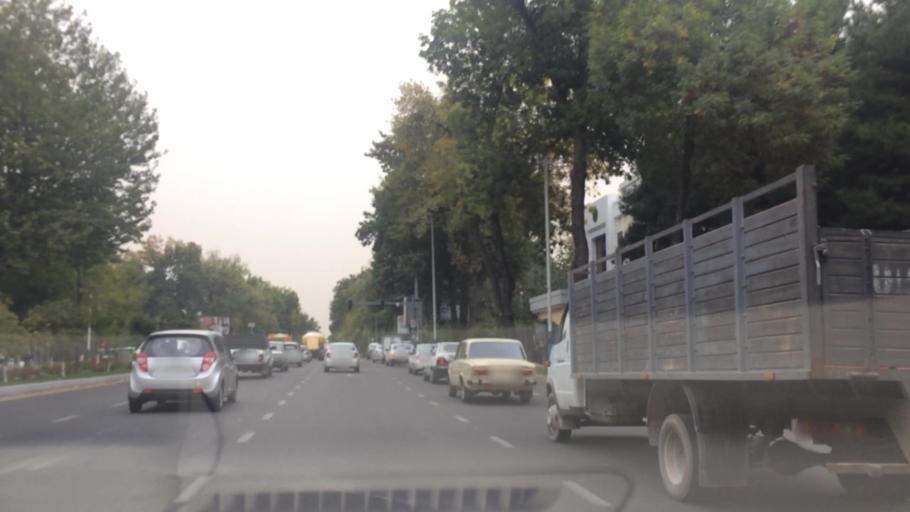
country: UZ
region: Toshkent Shahri
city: Tashkent
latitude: 41.3090
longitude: 69.2879
